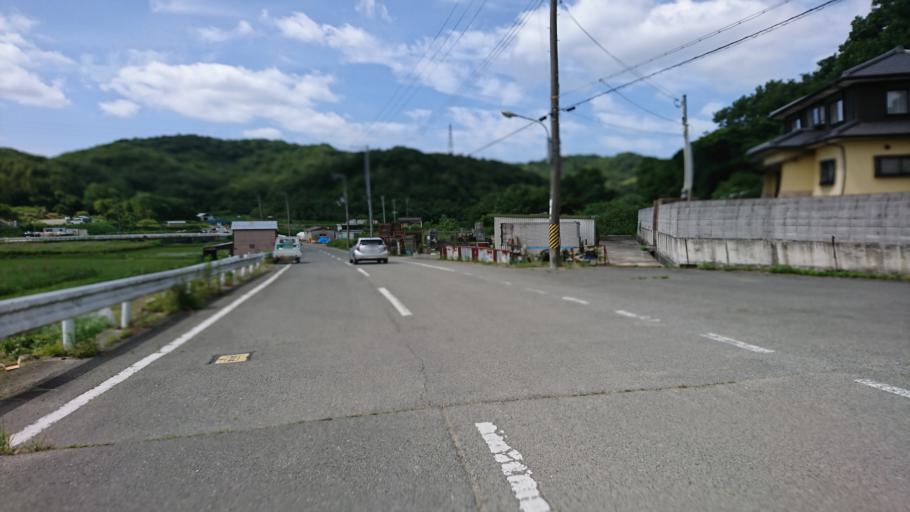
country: JP
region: Hyogo
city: Shirahamacho-usazakiminami
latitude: 34.7937
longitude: 134.7411
